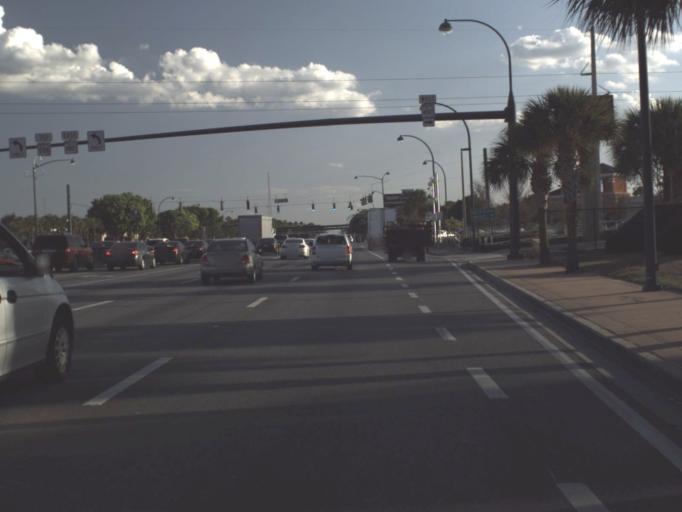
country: US
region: Florida
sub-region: Orange County
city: Sky Lake
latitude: 28.4516
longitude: -81.4006
